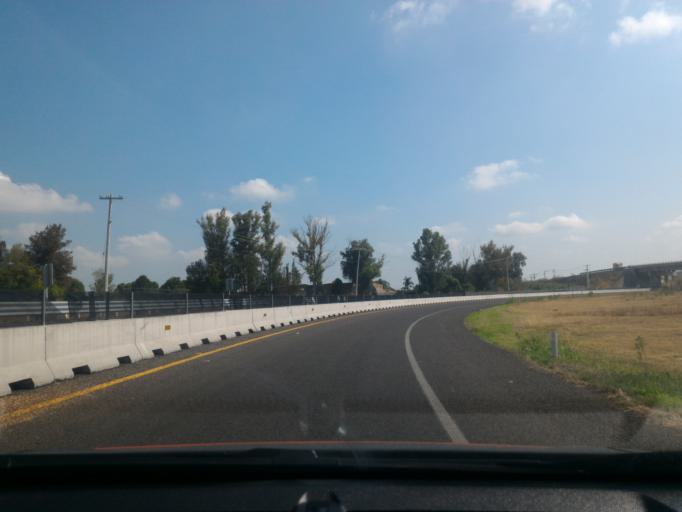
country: MX
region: Guanajuato
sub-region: Penjamo
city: Estacion la Piedad
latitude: 20.3931
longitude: -102.0008
